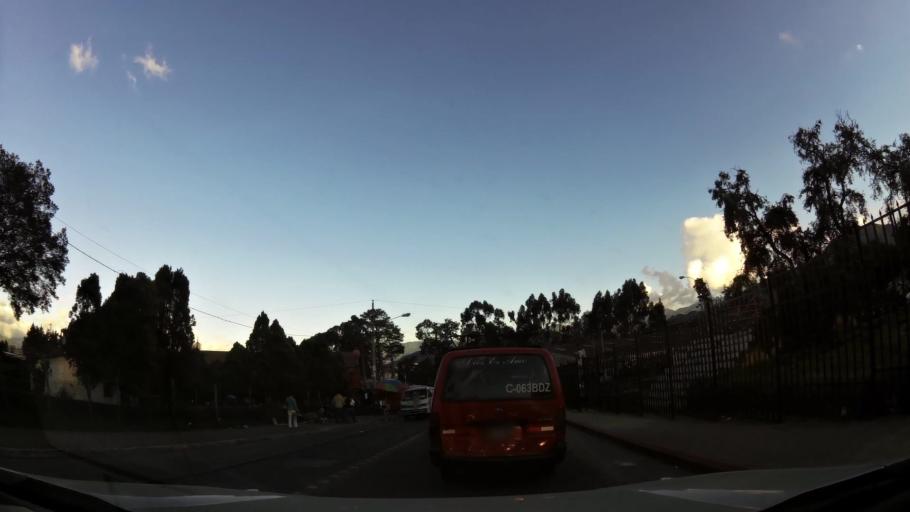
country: GT
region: Quetzaltenango
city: Quetzaltenango
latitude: 14.8461
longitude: -91.5330
